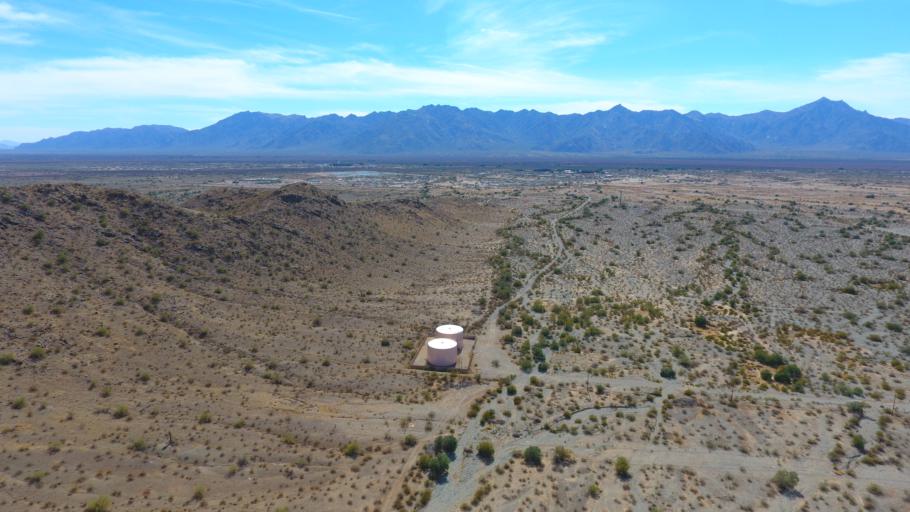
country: US
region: Arizona
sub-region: Maricopa County
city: Laveen
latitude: 33.3078
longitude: -112.1472
